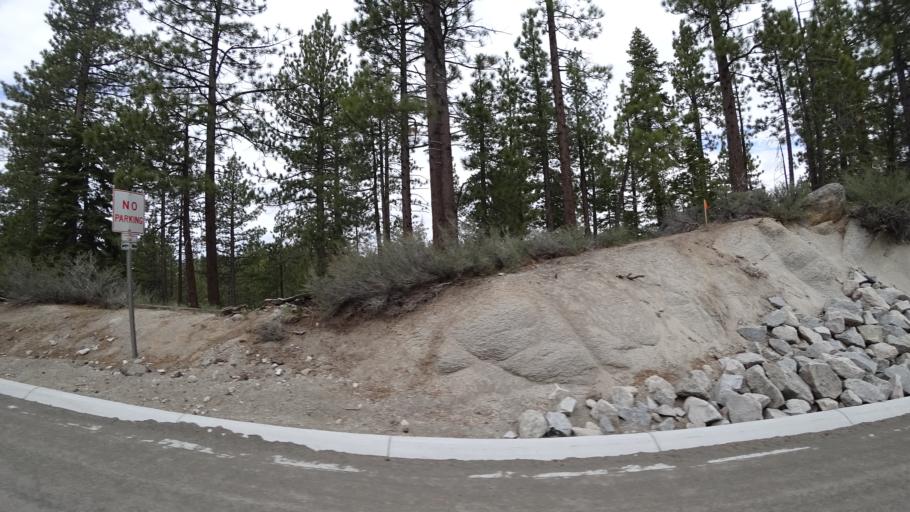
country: US
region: Nevada
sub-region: Washoe County
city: Incline Village
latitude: 39.1669
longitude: -119.9280
